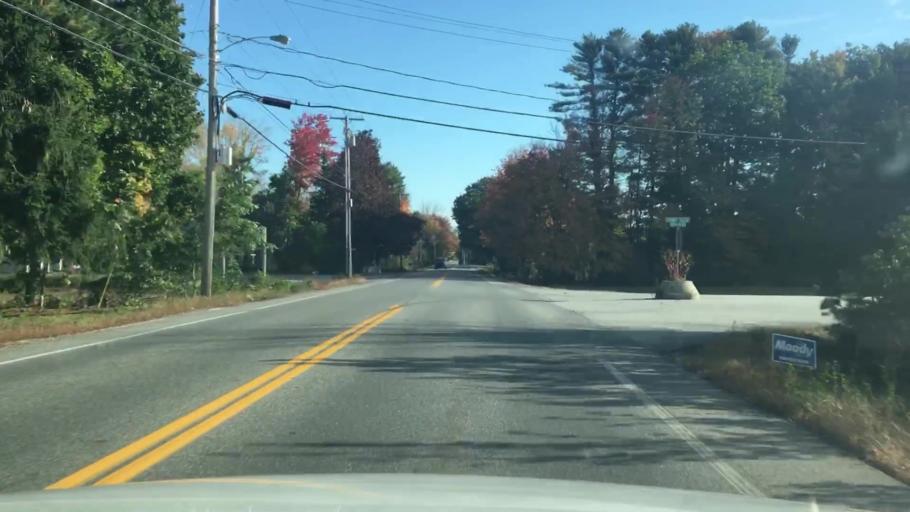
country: US
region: Maine
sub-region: Cumberland County
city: Gorham
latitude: 43.6251
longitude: -70.4568
